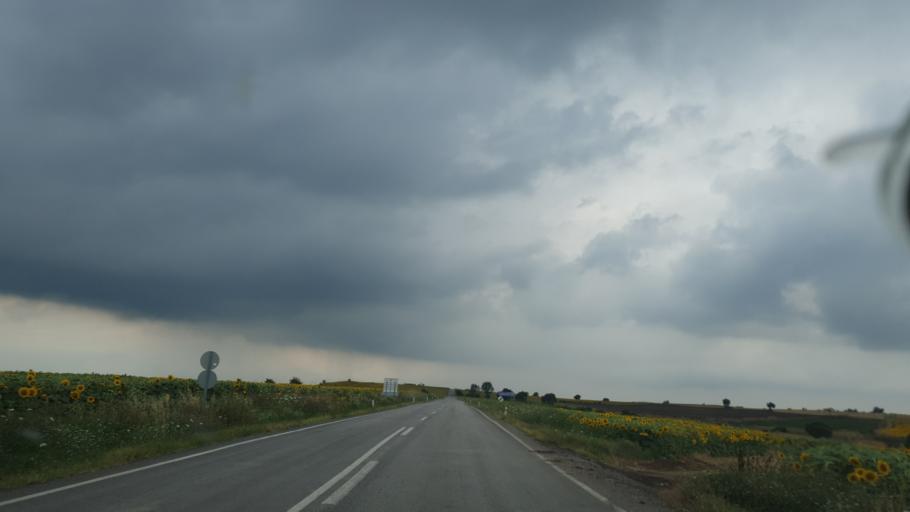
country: TR
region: Tekirdag
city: Hayrabolu
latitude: 41.2182
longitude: 26.9737
